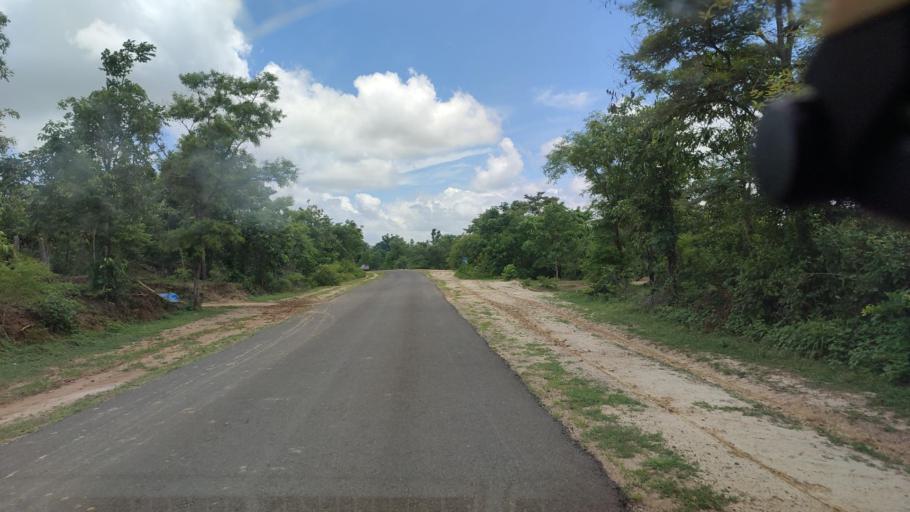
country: MM
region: Magway
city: Taungdwingyi
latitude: 20.1544
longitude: 95.5804
